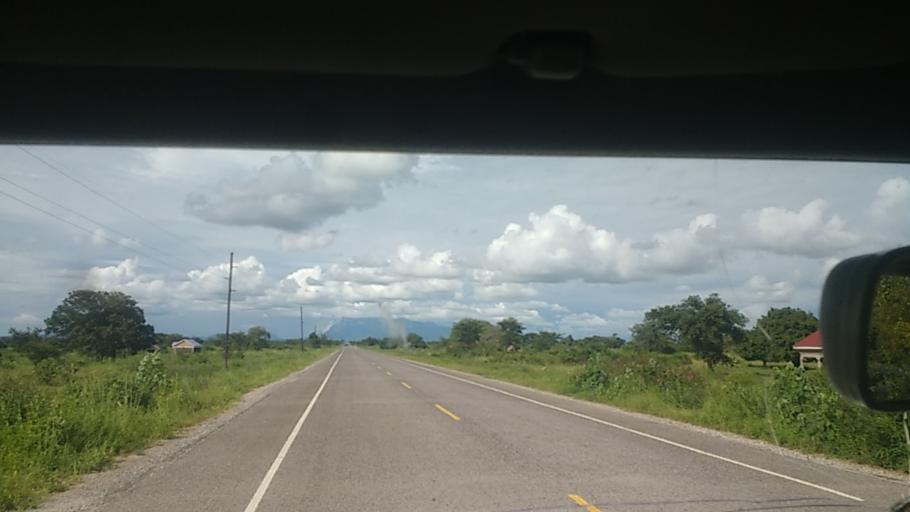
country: UG
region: Eastern Region
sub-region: Katakwi District
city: Katakwi
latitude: 1.9160
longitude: 34.0431
